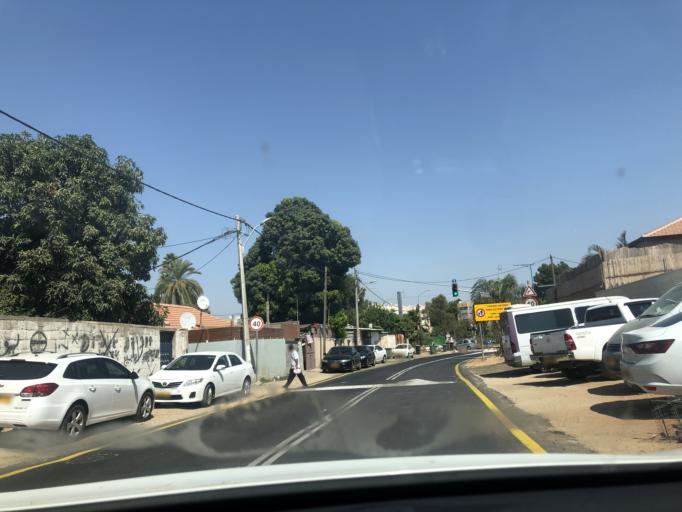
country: IL
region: Central District
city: Lod
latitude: 31.9502
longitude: 34.8802
